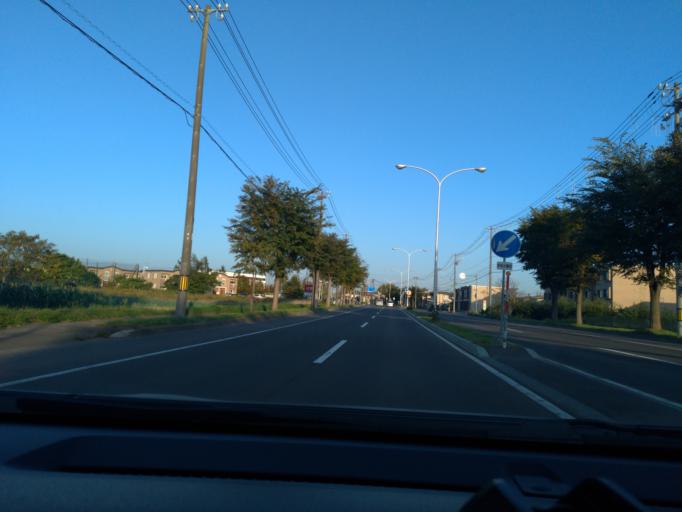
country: JP
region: Hokkaido
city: Ishikari
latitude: 43.1585
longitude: 141.3563
